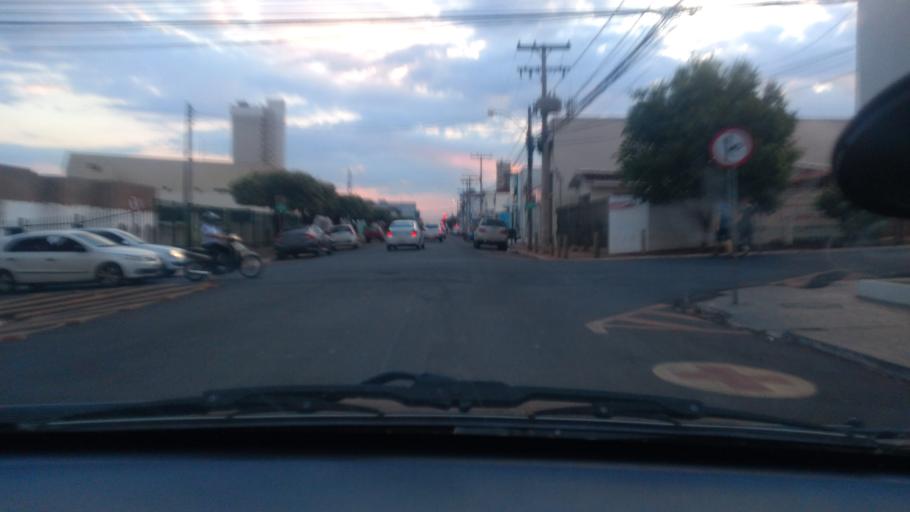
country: BR
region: Goias
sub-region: Santa Helena De Goias
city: Santa Helena de Goias
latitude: -17.7954
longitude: -50.9279
